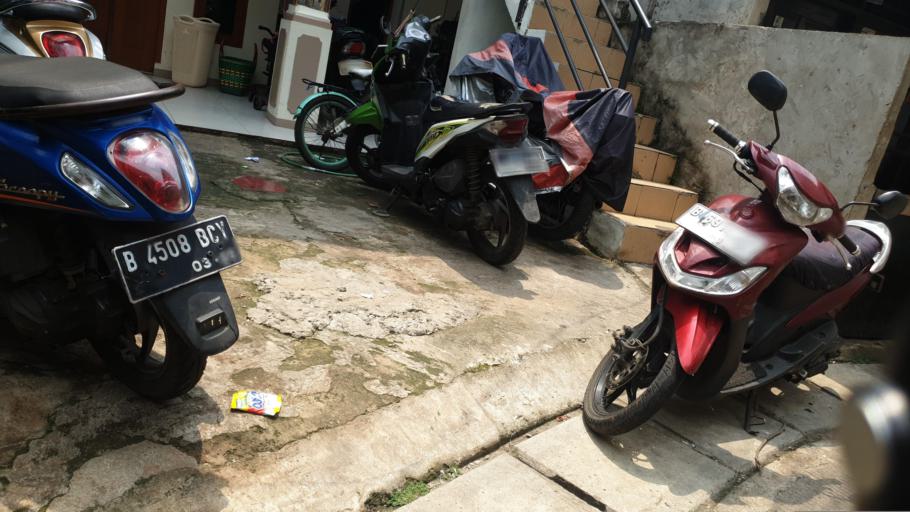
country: ID
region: West Java
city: Ciputat
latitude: -6.1955
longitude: 106.7539
